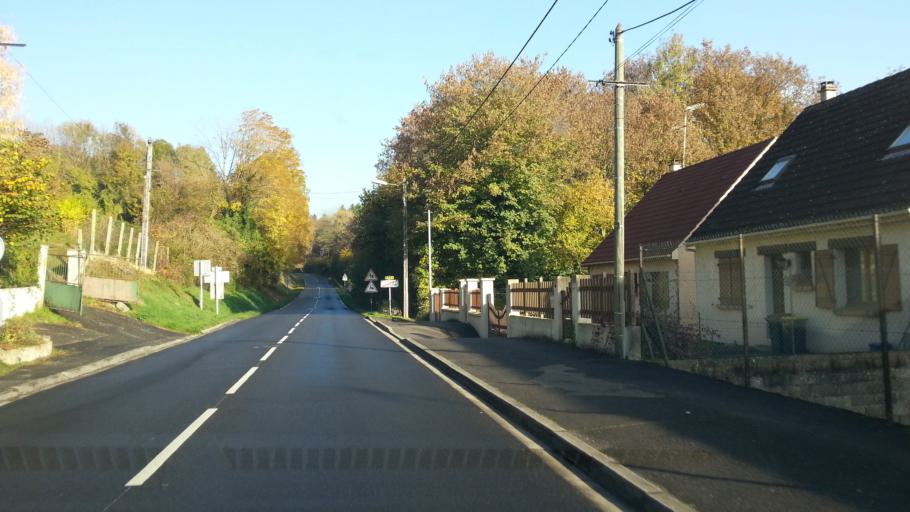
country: FR
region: Picardie
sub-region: Departement de l'Oise
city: Cires-les-Mello
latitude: 49.2818
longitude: 2.3604
